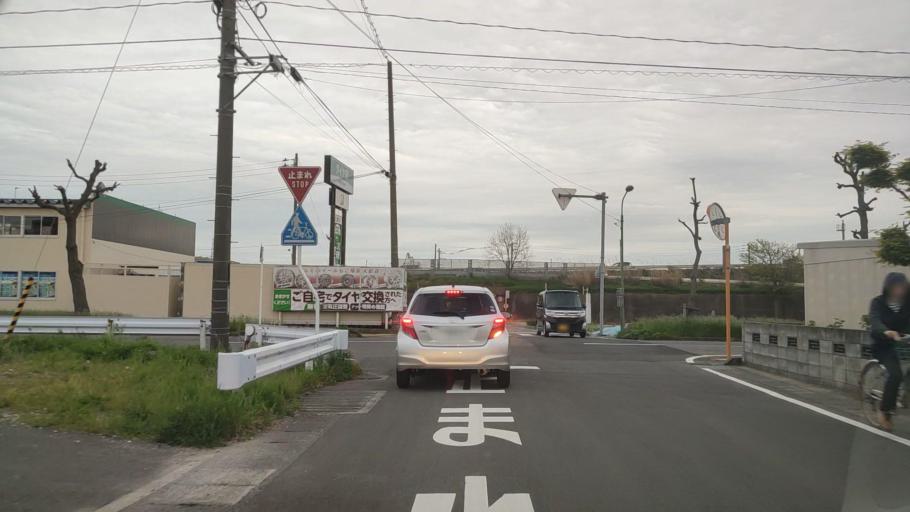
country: JP
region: Niigata
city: Kameda-honcho
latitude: 37.9136
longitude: 139.0991
